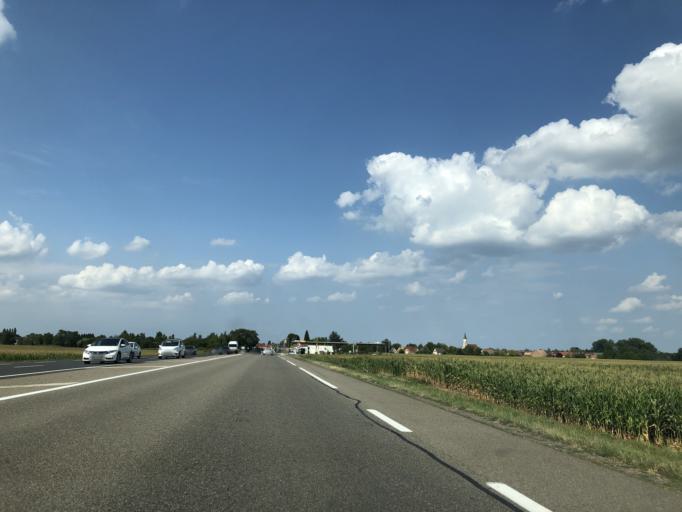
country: FR
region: Alsace
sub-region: Departement du Bas-Rhin
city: Lipsheim
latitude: 48.4829
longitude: 7.6724
